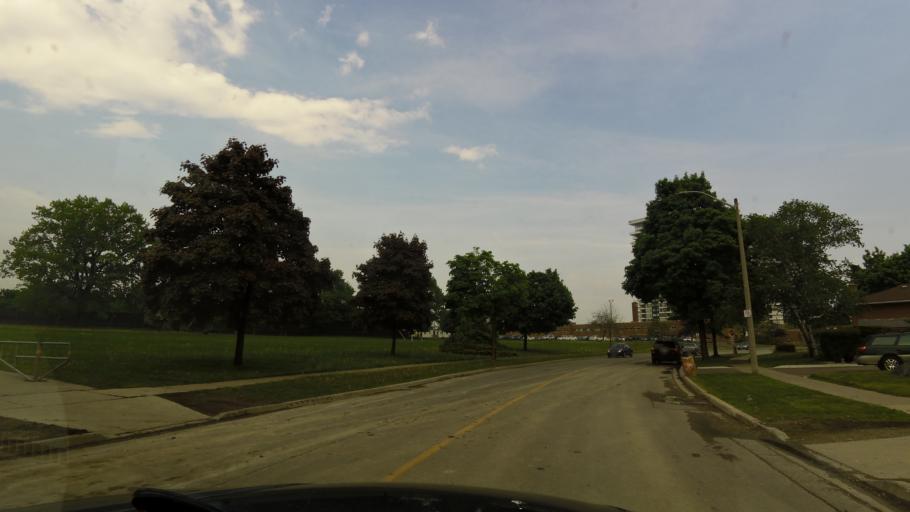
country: CA
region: Ontario
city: Etobicoke
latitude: 43.6169
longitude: -79.6002
